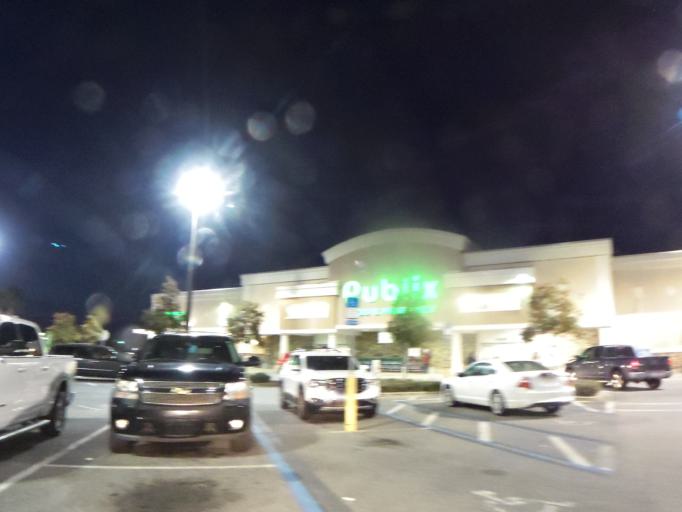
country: US
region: Florida
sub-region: Nassau County
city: Yulee
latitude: 30.6273
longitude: -81.5456
